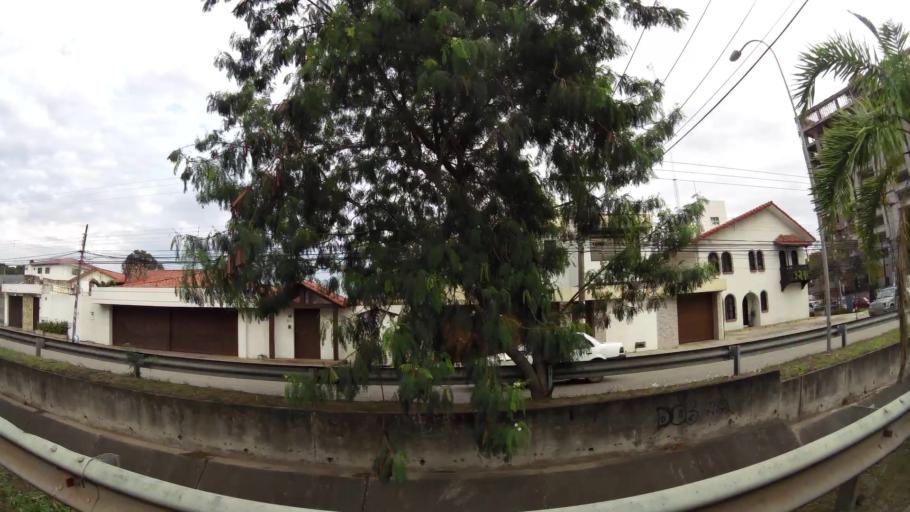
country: BO
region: Santa Cruz
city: Santa Cruz de la Sierra
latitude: -17.7642
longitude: -63.1763
